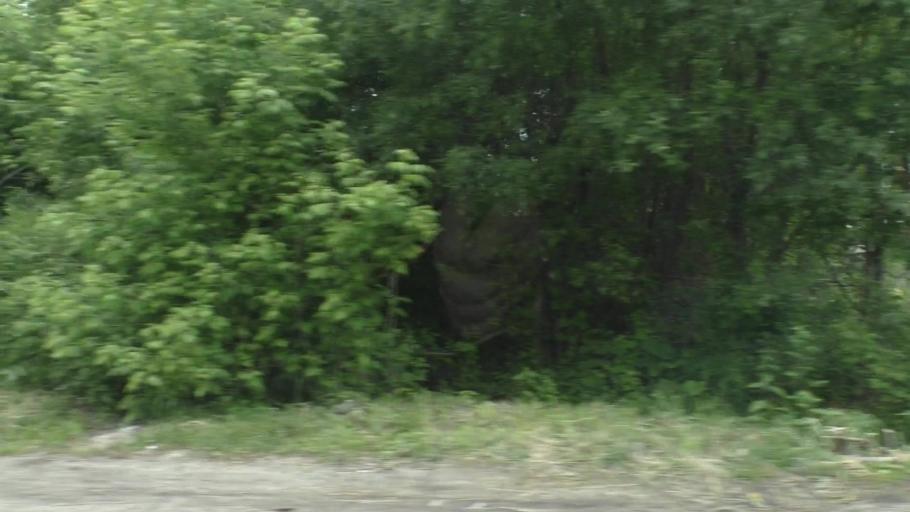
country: RU
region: Moskovskaya
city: Yegor'yevsk
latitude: 55.3964
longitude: 39.0151
